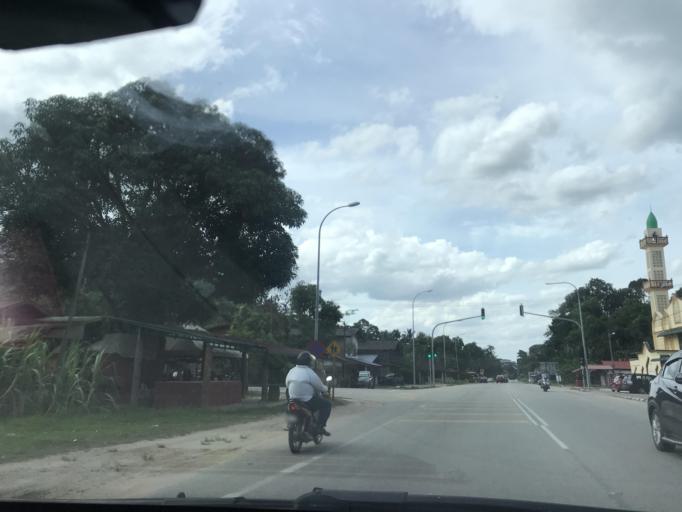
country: MY
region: Kelantan
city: Kampong Pangkal Kalong
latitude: 5.8834
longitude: 102.1773
